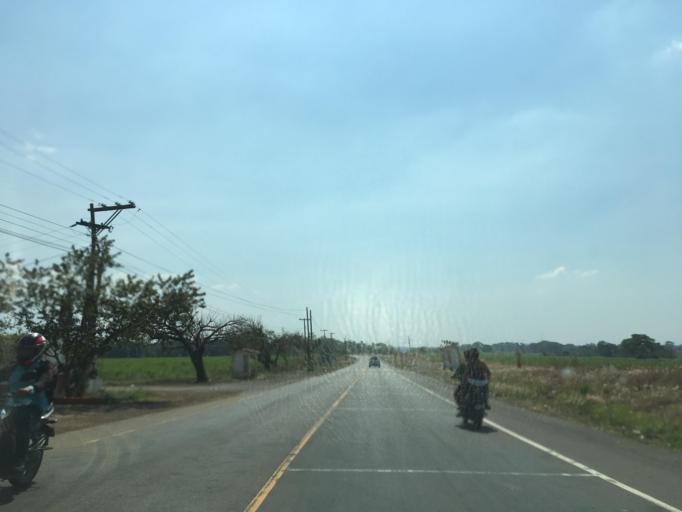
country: GT
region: Escuintla
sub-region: Municipio de Escuintla
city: Escuintla
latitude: 14.2753
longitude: -90.7599
